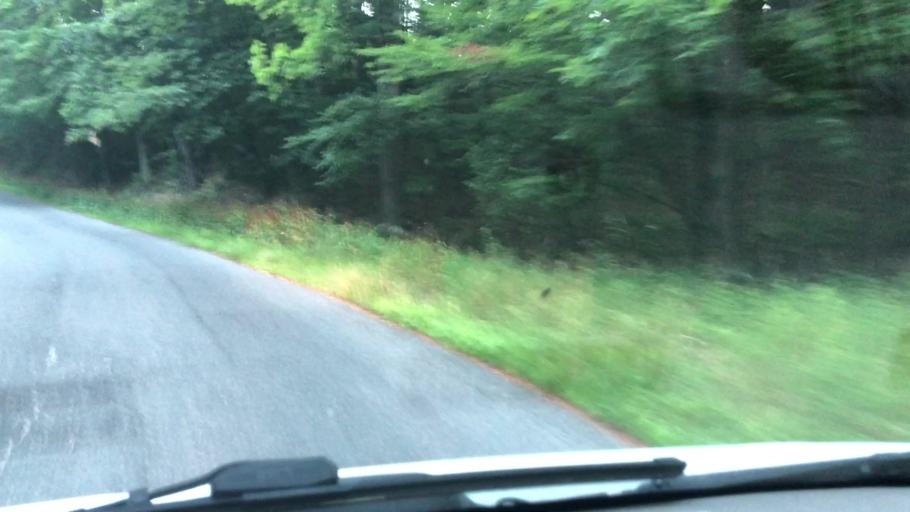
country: US
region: Massachusetts
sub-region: Hampshire County
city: Southampton
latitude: 42.2448
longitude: -72.7056
